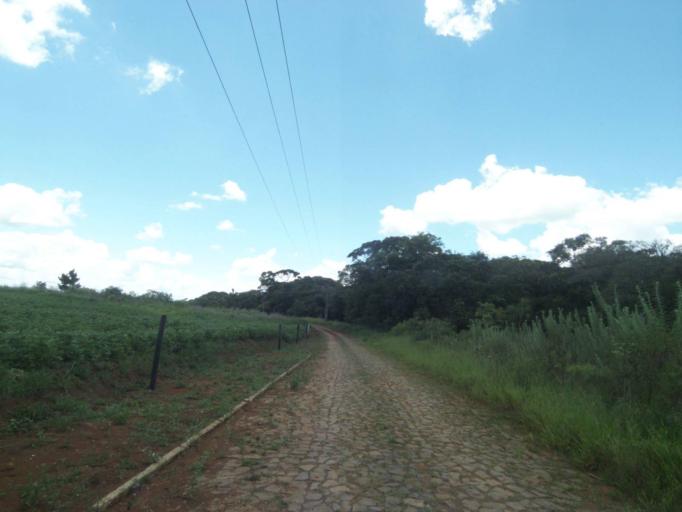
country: BR
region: Parana
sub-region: Pinhao
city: Pinhao
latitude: -25.7904
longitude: -52.0792
